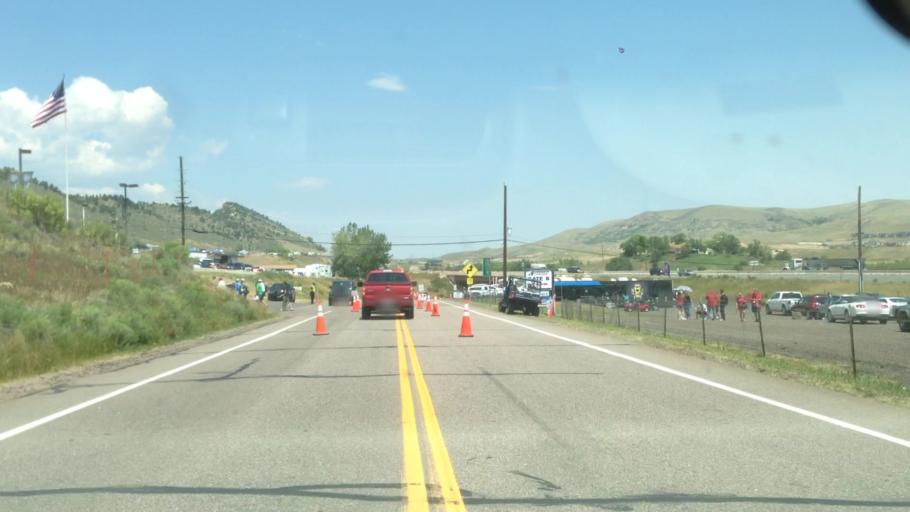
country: US
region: Colorado
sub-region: Jefferson County
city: Indian Hills
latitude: 39.6592
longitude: -105.1842
